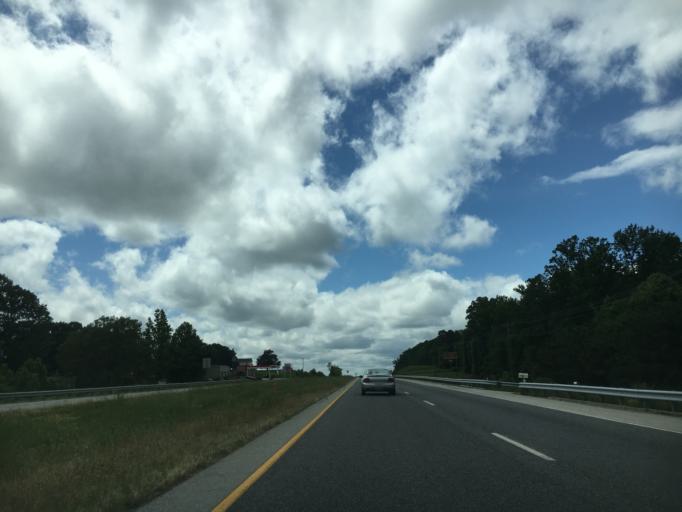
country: US
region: Virginia
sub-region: Mecklenburg County
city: Boydton
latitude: 36.6717
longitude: -78.2853
